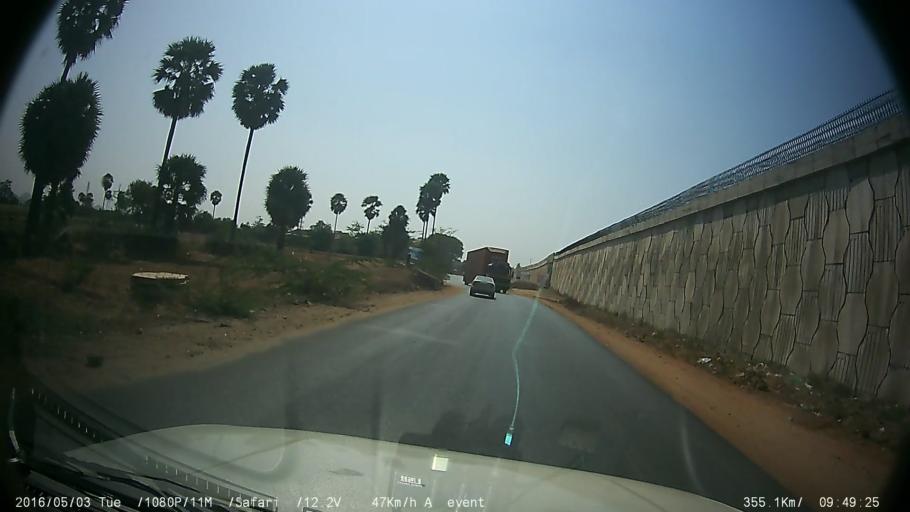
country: IN
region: Tamil Nadu
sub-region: Coimbatore
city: Madukkarai
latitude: 10.8720
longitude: 76.8955
